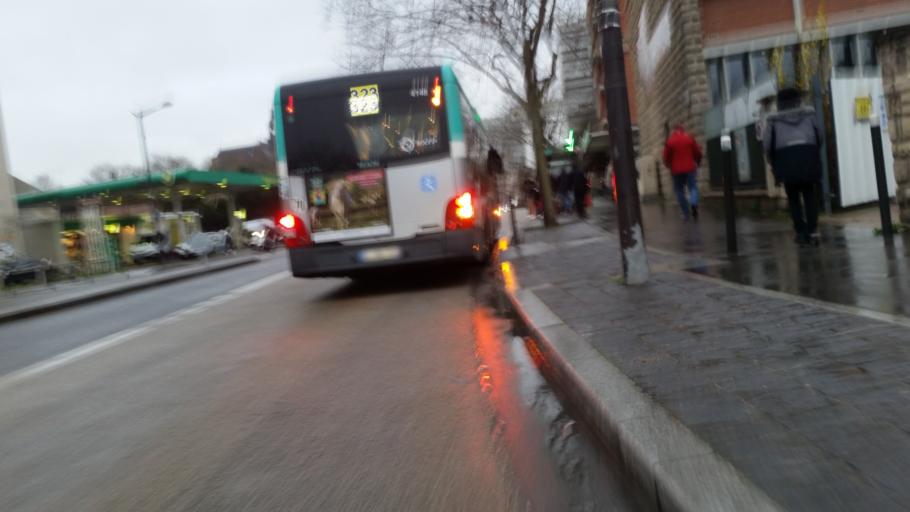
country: FR
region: Ile-de-France
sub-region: Departement du Val-de-Marne
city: Ivry-sur-Seine
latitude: 48.8139
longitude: 2.3892
